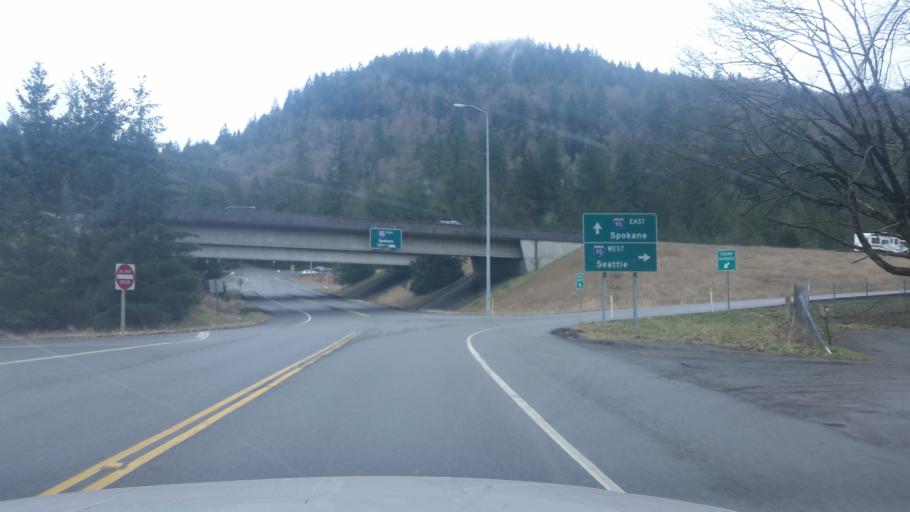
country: US
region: Washington
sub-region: King County
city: Issaquah
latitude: 47.5323
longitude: -121.9800
